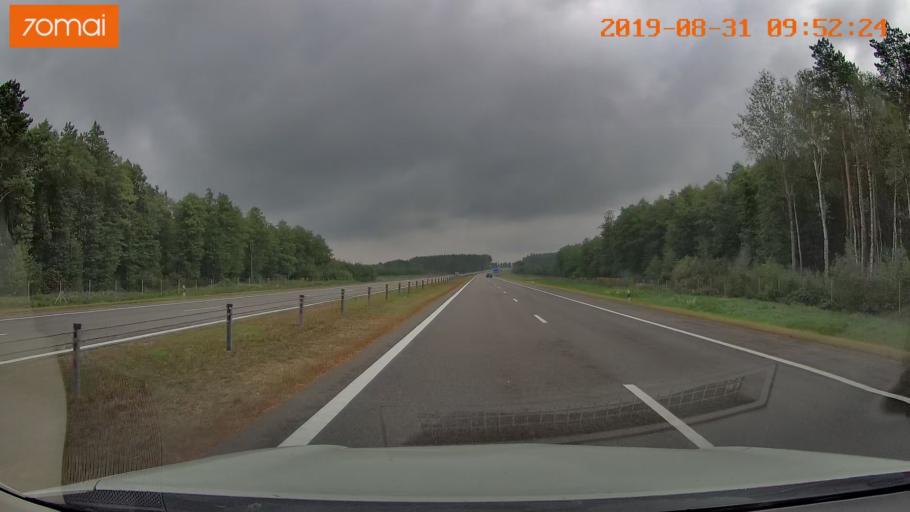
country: BY
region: Mogilev
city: Byalynichy
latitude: 53.9785
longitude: 29.7755
